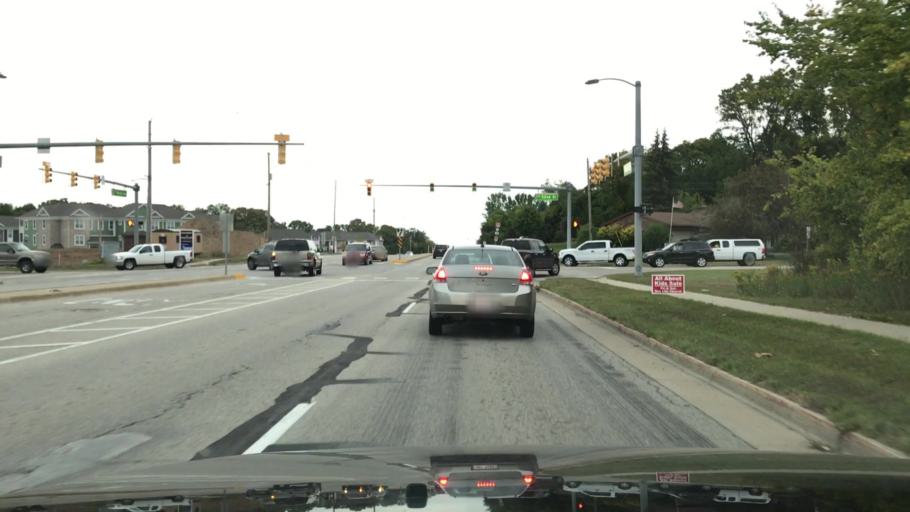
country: US
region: Michigan
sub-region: Kent County
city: Grandville
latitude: 42.8699
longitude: -85.7623
